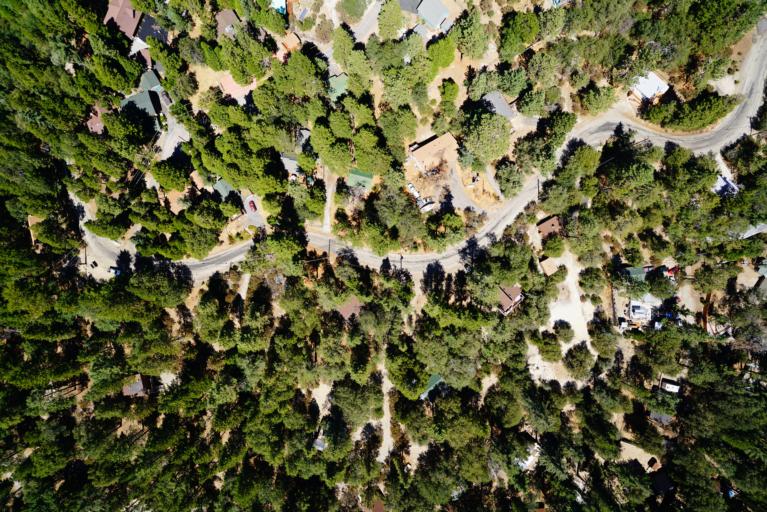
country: US
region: California
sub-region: Riverside County
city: Idyllwild-Pine Cove
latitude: 33.7587
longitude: -116.7441
